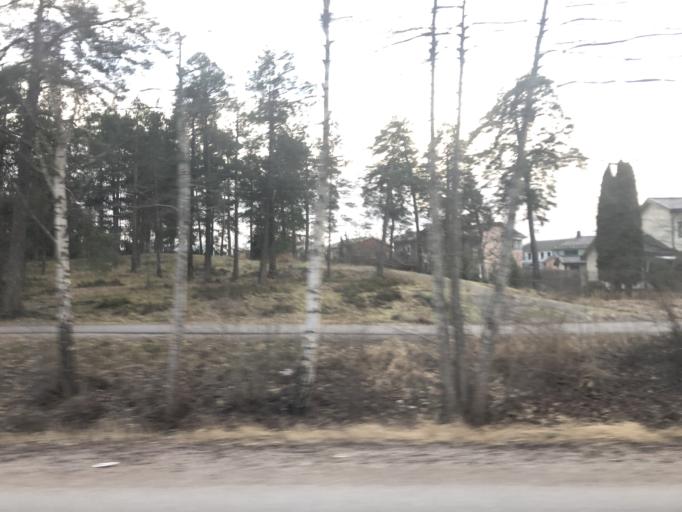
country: SE
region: Stockholm
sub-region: Jarfalla Kommun
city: Jakobsberg
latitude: 59.4031
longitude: 17.7992
